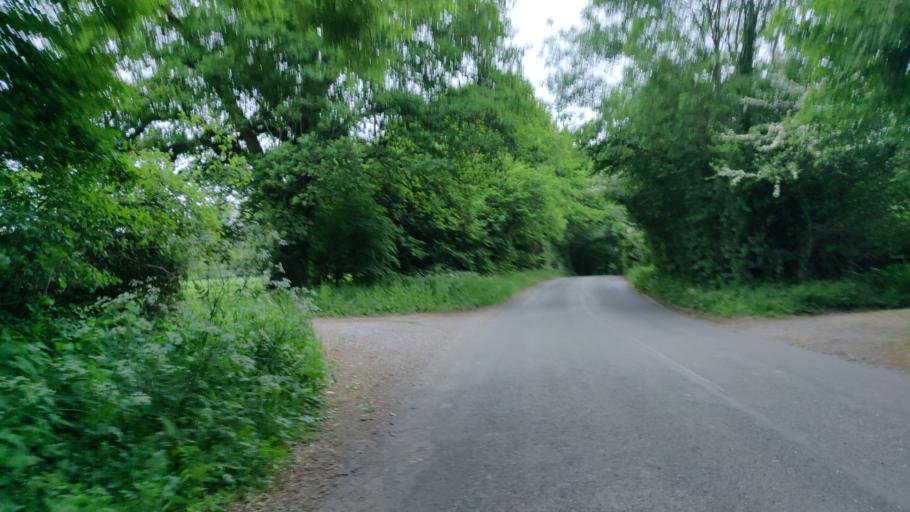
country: GB
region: England
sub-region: West Sussex
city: Partridge Green
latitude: 51.0020
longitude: -0.3078
